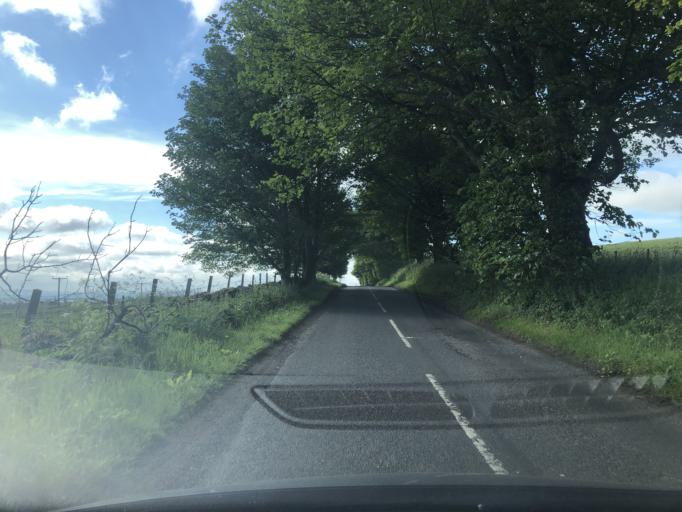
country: GB
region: Scotland
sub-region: Angus
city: Kirriemuir
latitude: 56.7367
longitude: -3.0051
